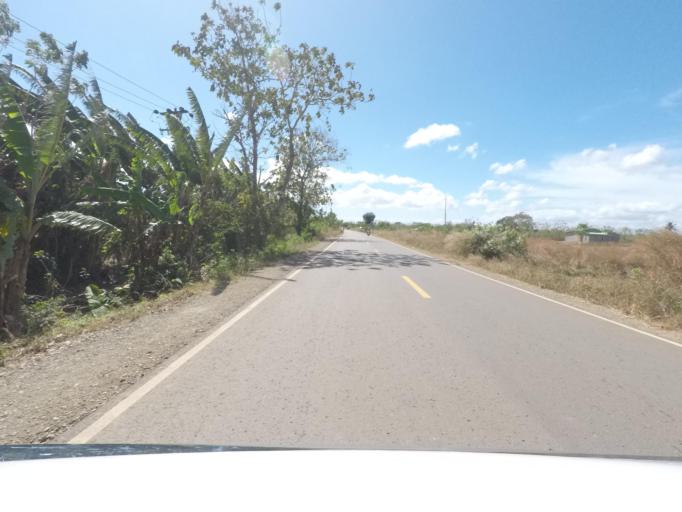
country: TL
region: Baucau
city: Baucau
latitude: -8.4898
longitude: 126.3699
